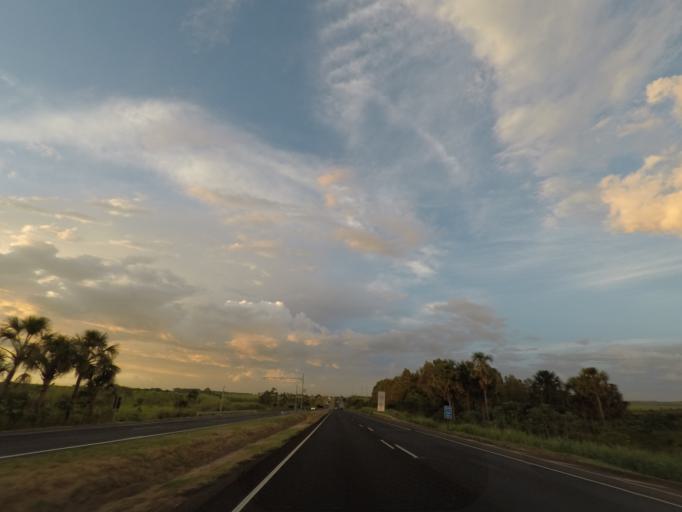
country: BR
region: Minas Gerais
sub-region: Uberaba
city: Uberaba
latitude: -19.6596
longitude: -48.0024
